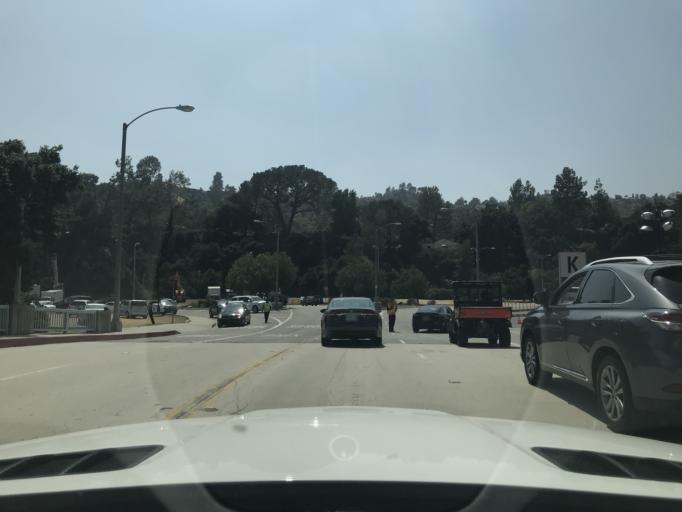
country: US
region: California
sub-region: Los Angeles County
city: Pasadena
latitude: 34.1561
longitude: -118.1680
